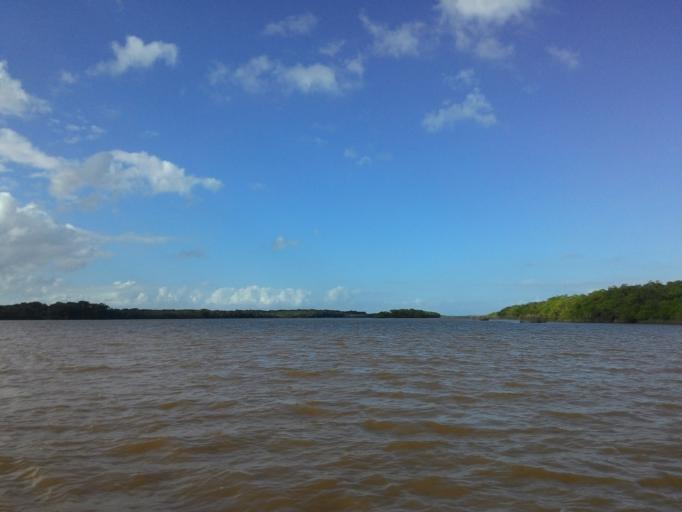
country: BR
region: Sao Paulo
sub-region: Pariquera-Acu
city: Pariquera Acu
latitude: -24.8424
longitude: -47.7431
